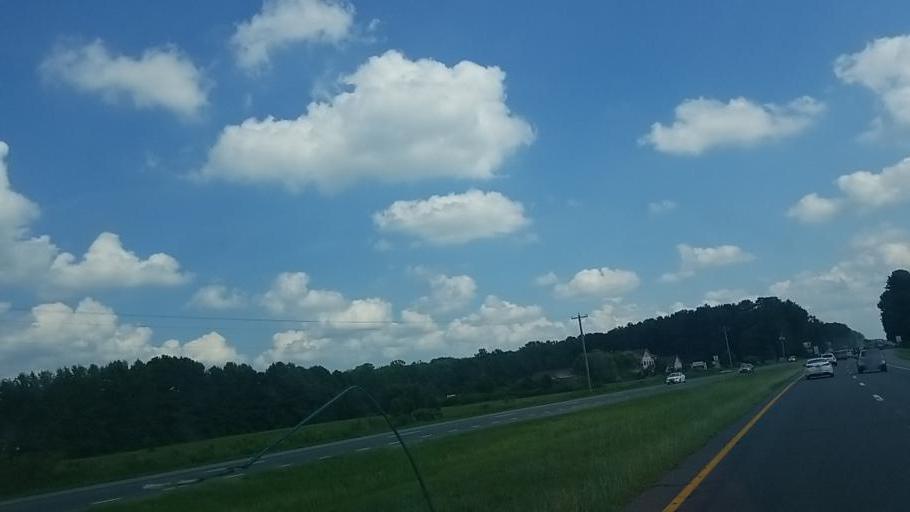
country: US
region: Delaware
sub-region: Sussex County
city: Georgetown
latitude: 38.6778
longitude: -75.3922
